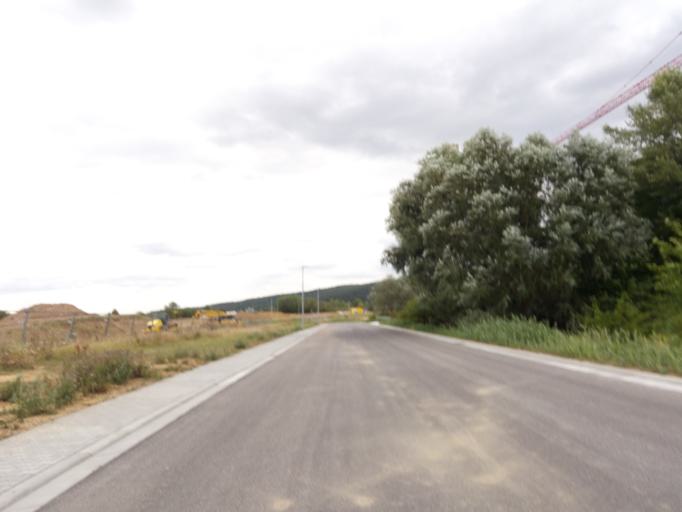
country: DE
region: Rheinland-Pfalz
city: Waldlaubersheim
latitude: 49.9234
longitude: 7.8216
